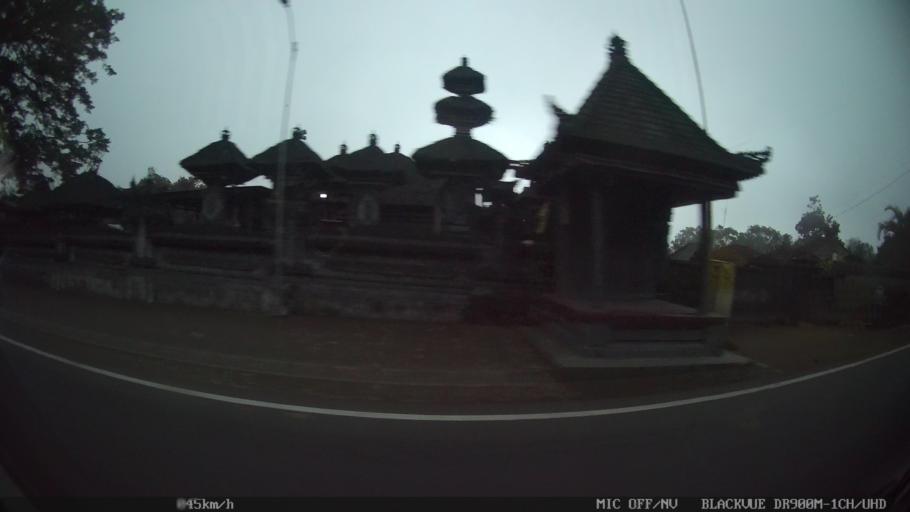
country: ID
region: Bali
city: Banjar Taro Kelod
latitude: -8.3083
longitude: 115.3051
